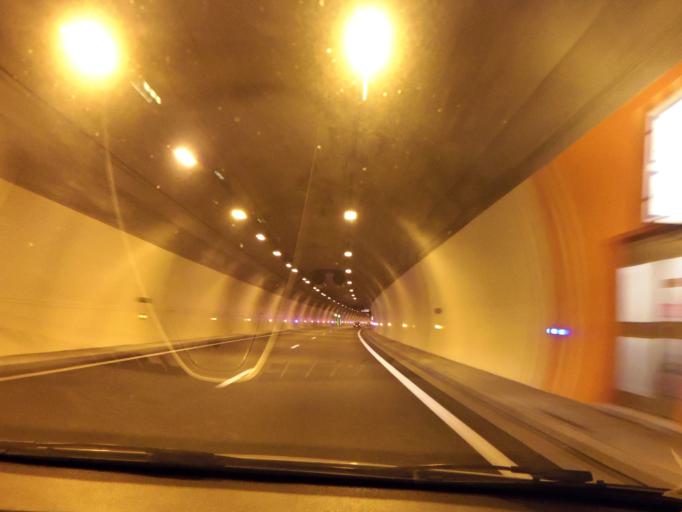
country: FR
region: Rhone-Alpes
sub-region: Departement du Rhone
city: Tarare
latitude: 45.8828
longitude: 4.4274
